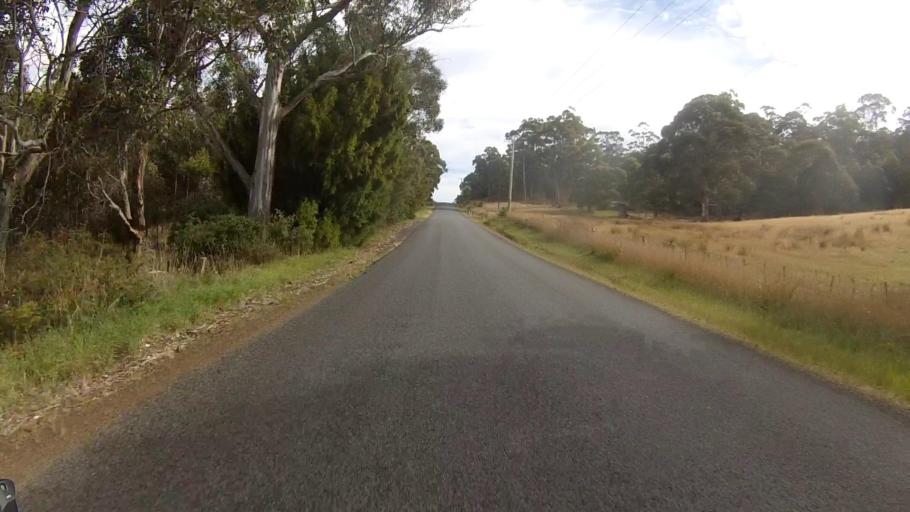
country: AU
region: Tasmania
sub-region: Sorell
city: Sorell
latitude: -42.8033
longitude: 147.7933
